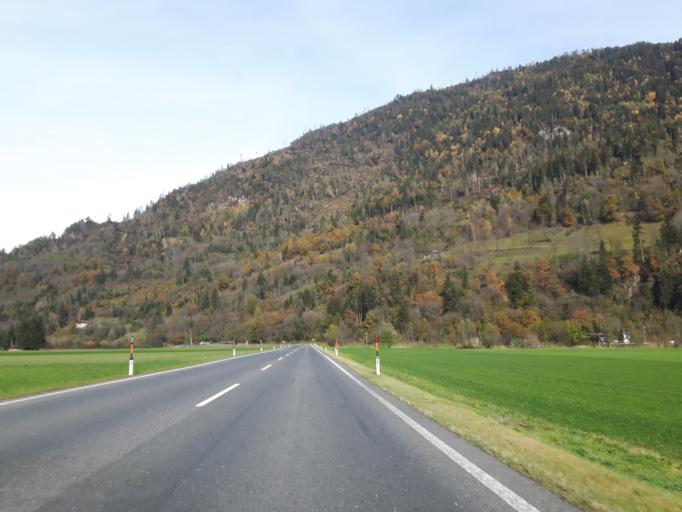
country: AT
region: Tyrol
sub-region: Politischer Bezirk Lienz
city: Lavant
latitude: 46.7978
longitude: 12.8741
